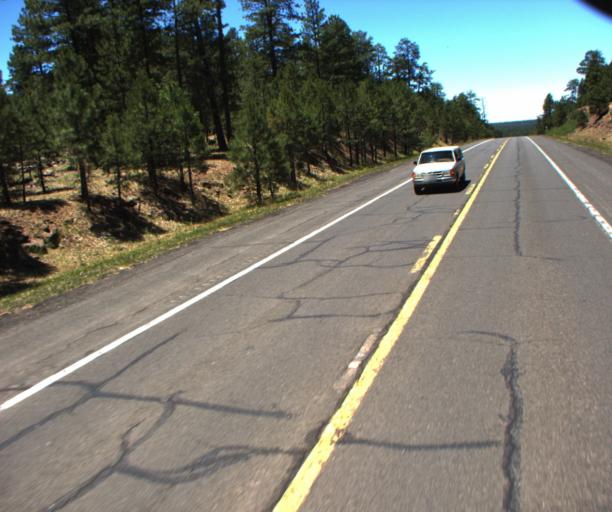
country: US
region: Arizona
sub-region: Gila County
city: Pine
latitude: 34.5526
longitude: -111.2951
